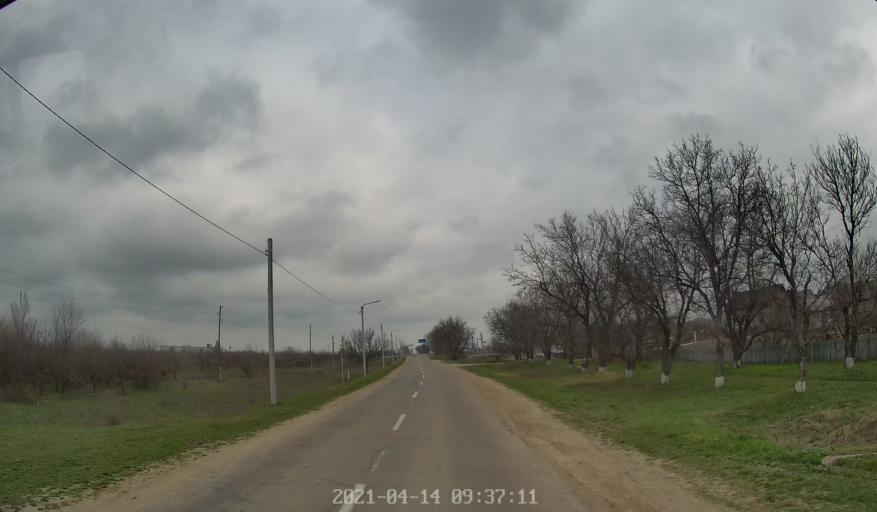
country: MD
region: Chisinau
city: Vadul lui Voda
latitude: 47.1167
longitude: 29.1112
